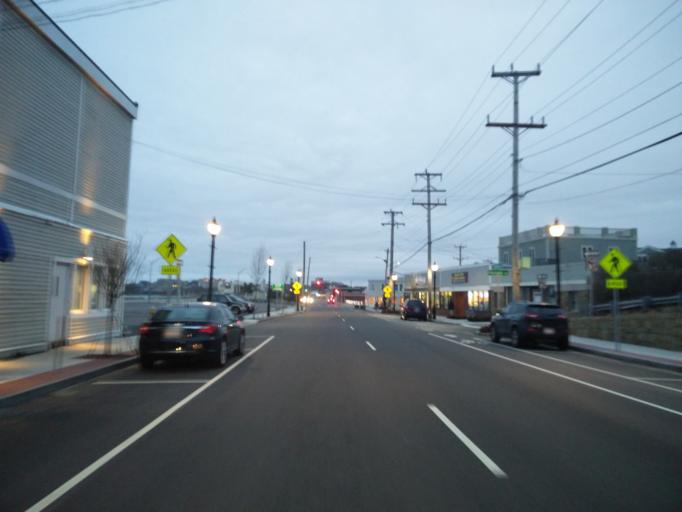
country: US
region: Massachusetts
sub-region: Plymouth County
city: Hingham
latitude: 42.2735
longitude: -70.8604
